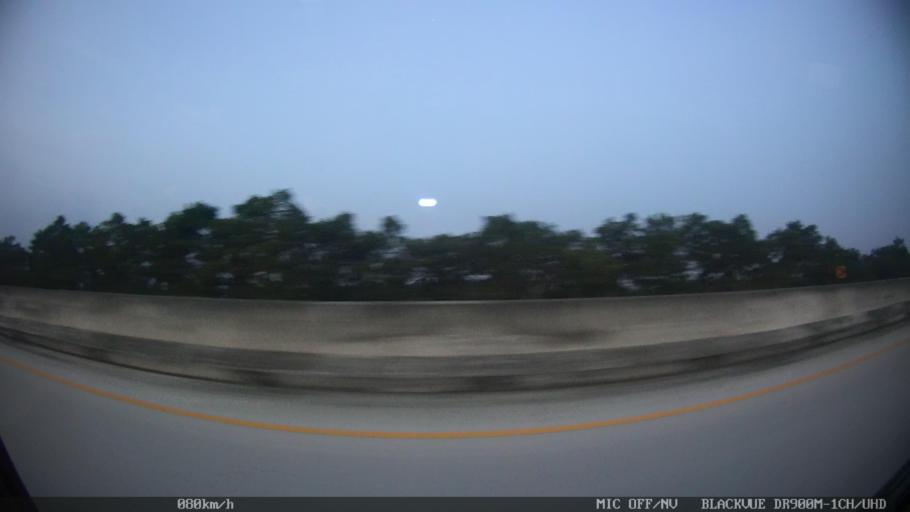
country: ID
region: Lampung
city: Sidorejo
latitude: -5.5707
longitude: 105.5383
